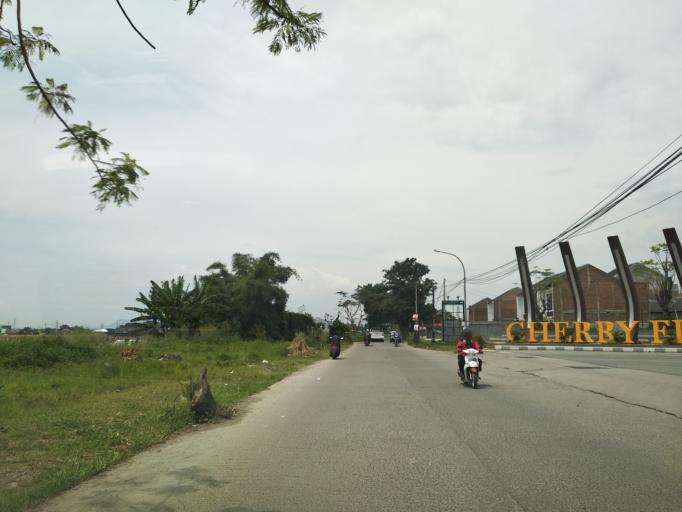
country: ID
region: West Java
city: Pameungpeuk
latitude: -6.9710
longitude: 107.6427
